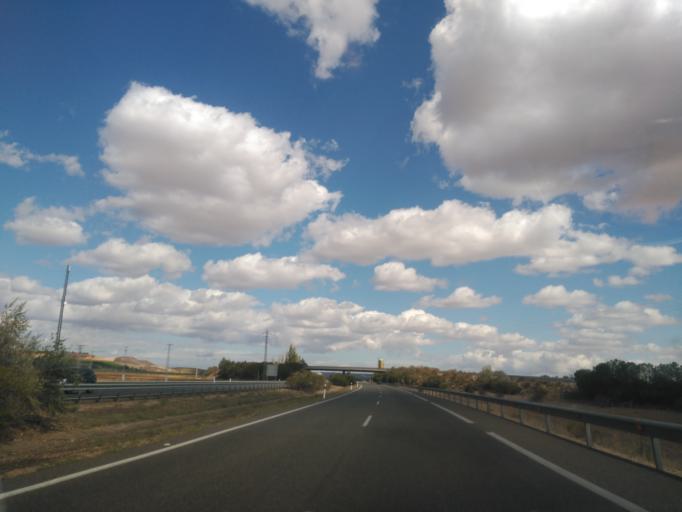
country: ES
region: Castille and Leon
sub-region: Provincia de Palencia
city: Reinoso de Cerrato
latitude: 41.9883
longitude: -4.4159
